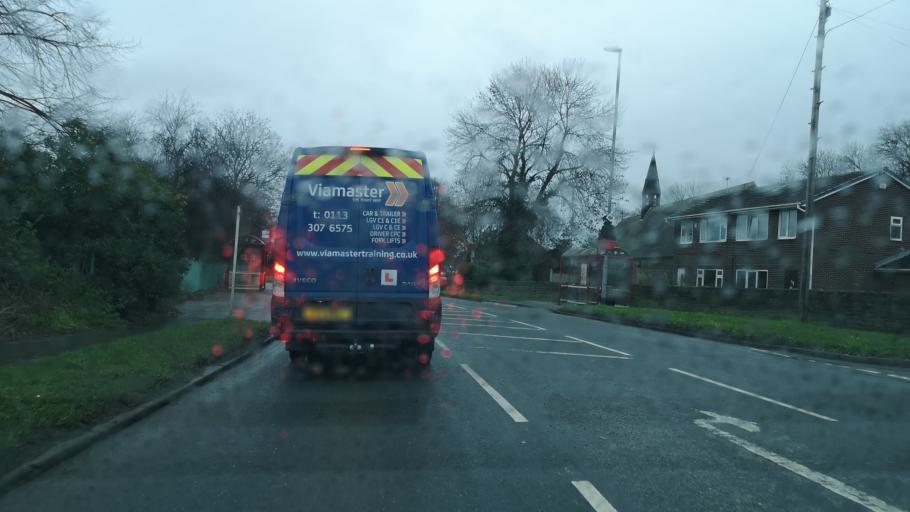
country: GB
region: England
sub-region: City and Borough of Wakefield
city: Sharlston
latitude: 53.6669
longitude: -1.4165
